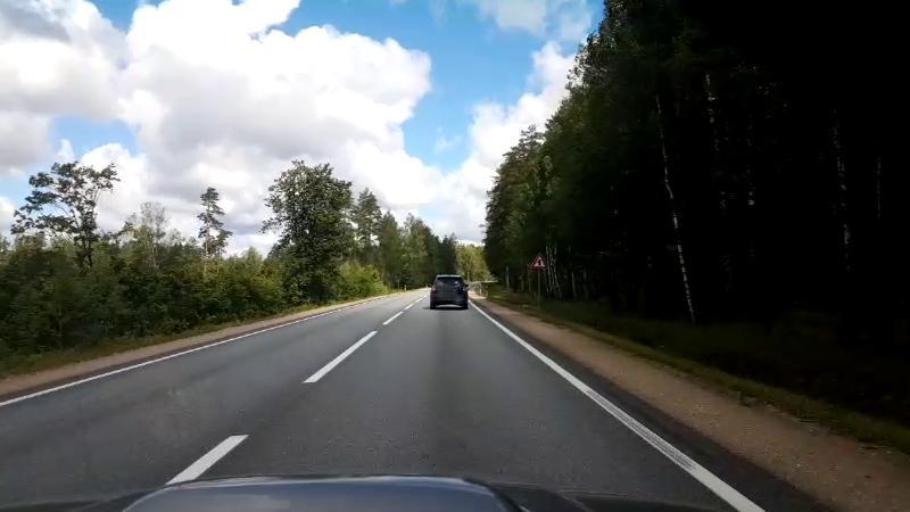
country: LV
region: Riga
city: Bergi
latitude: 56.9511
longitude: 24.3781
